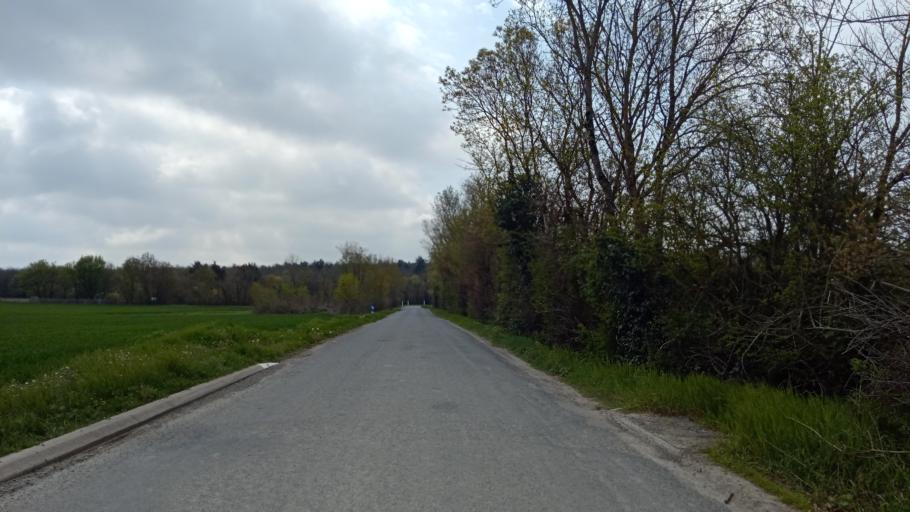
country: FR
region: Poitou-Charentes
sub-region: Departement de la Charente-Maritime
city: Verines
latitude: 46.1497
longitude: -0.9361
